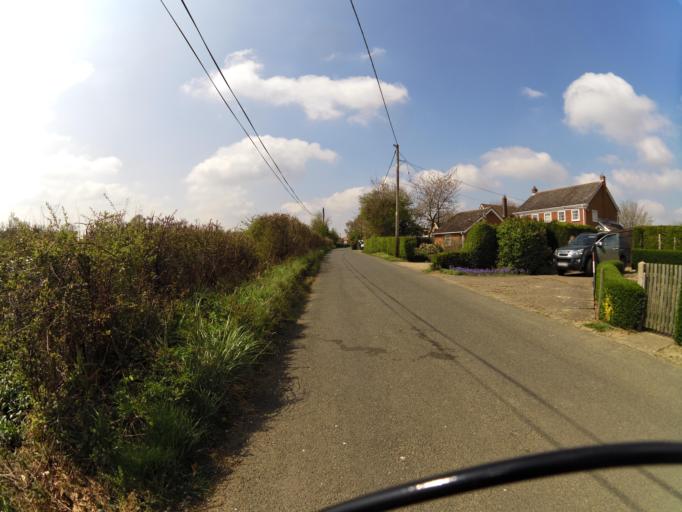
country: GB
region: England
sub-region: Suffolk
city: Hadleigh
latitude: 52.0799
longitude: 0.9925
